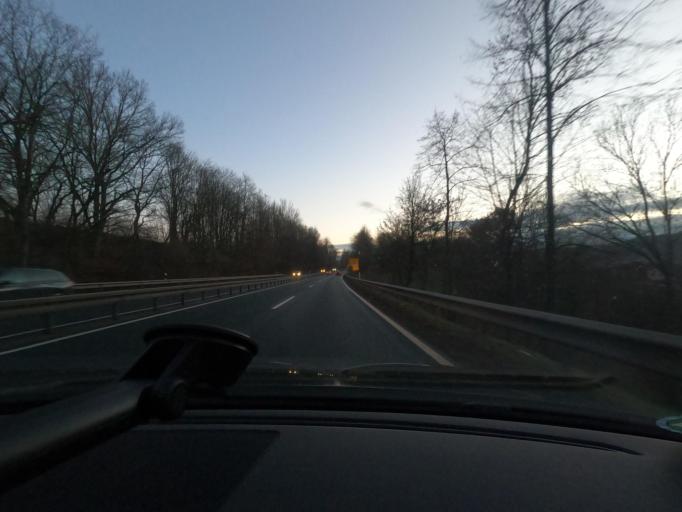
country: DE
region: Lower Saxony
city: Badenhausen
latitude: 51.7669
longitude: 10.2171
